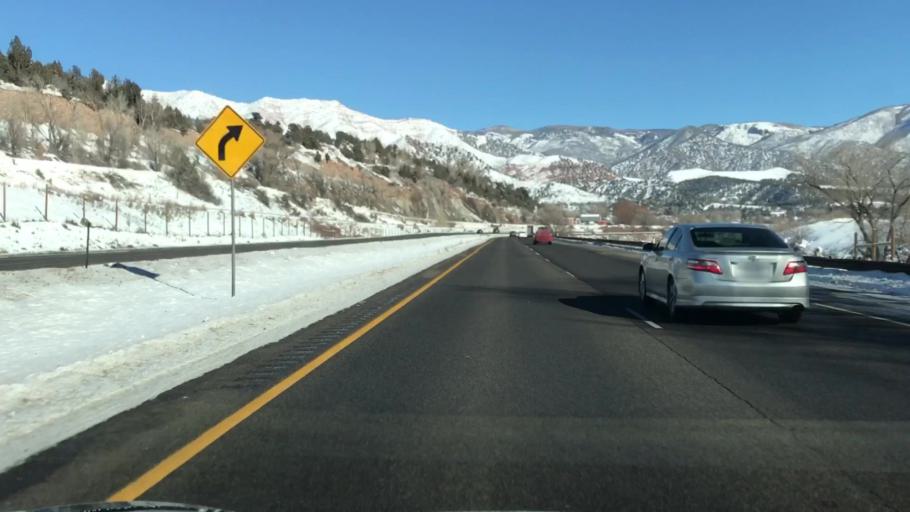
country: US
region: Colorado
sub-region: Garfield County
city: New Castle
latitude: 39.5690
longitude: -107.4852
